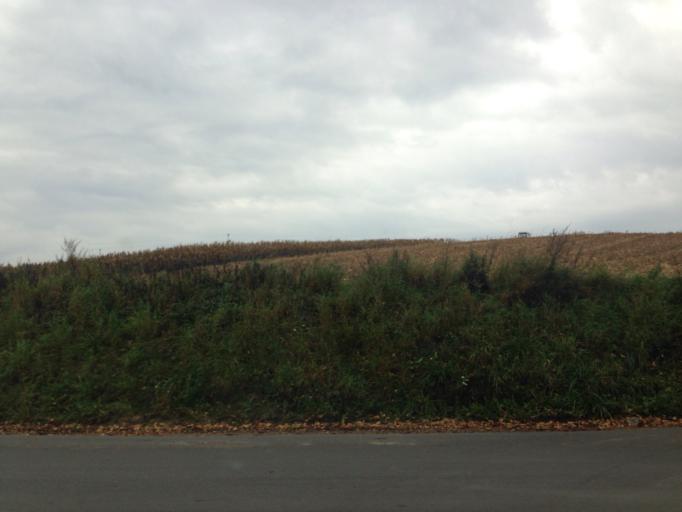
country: PL
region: Kujawsko-Pomorskie
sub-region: Powiat brodnicki
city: Brzozie
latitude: 53.3128
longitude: 19.5707
